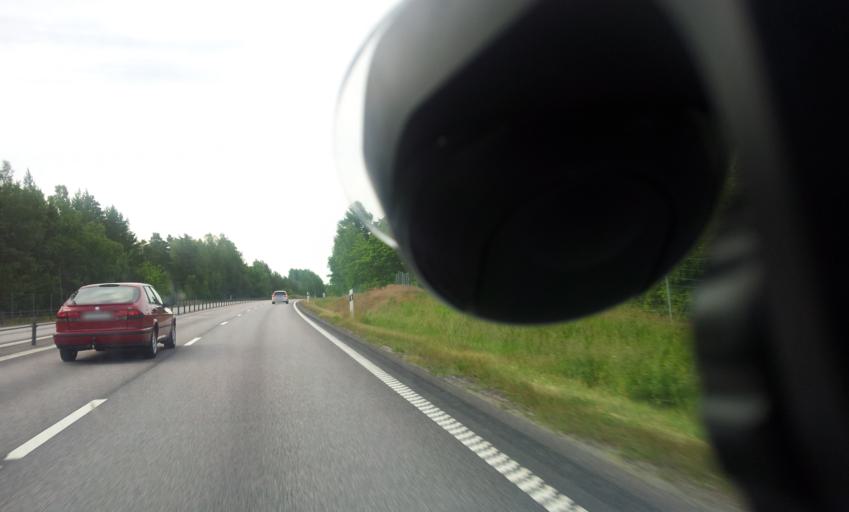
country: SE
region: Kalmar
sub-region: Oskarshamns Kommun
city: Paskallavik
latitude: 57.1492
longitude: 16.4661
